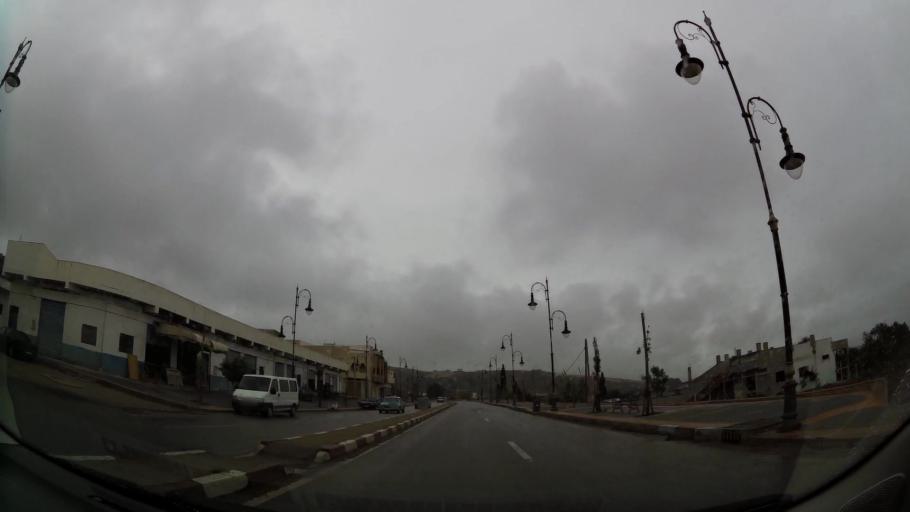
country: MA
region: Taza-Al Hoceima-Taounate
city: Imzourene
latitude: 35.1757
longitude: -3.8746
